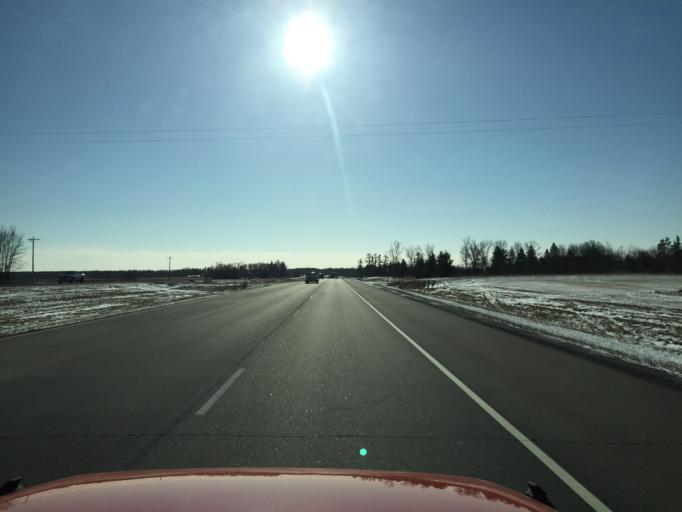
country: US
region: Minnesota
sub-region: Mille Lacs County
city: Milaca
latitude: 45.8415
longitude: -93.6618
